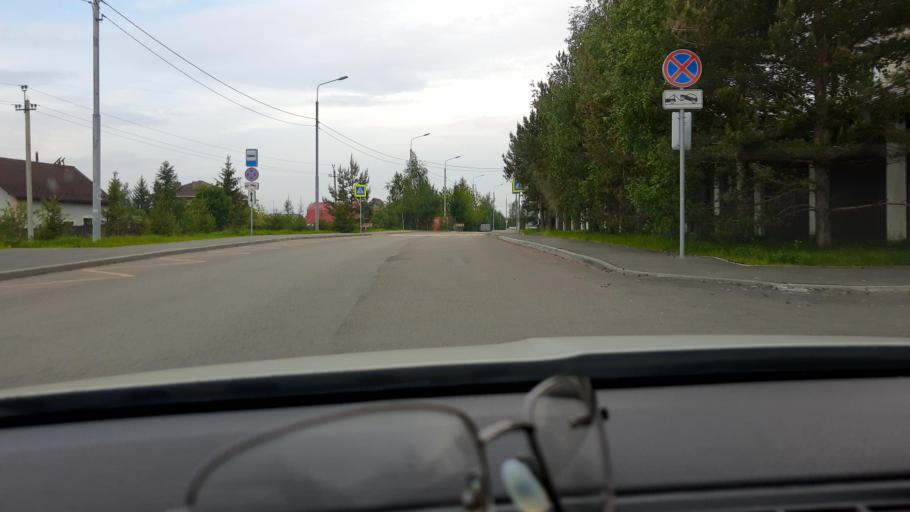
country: RU
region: Moskovskaya
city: Poselok Mar'ino
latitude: 55.5229
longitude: 37.3116
